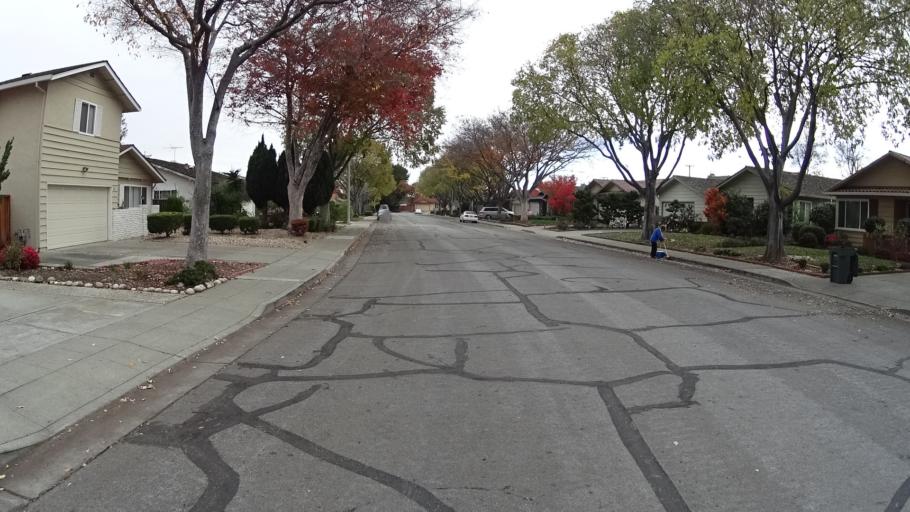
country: US
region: California
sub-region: Santa Clara County
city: Sunnyvale
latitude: 37.3639
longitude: -122.0171
